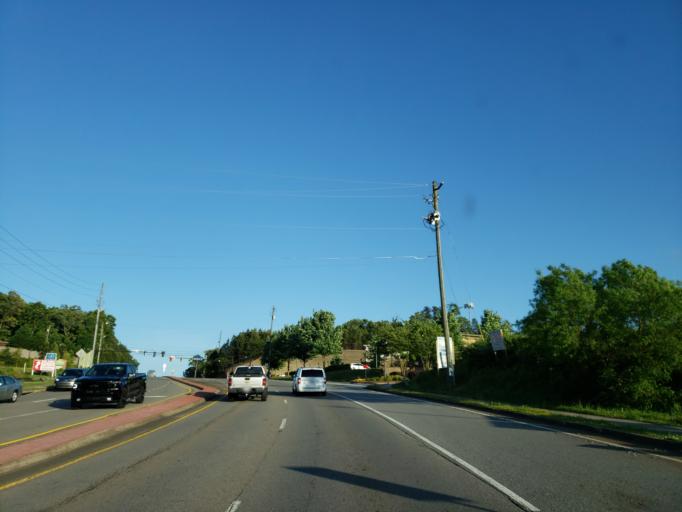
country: US
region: Georgia
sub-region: Cherokee County
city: Holly Springs
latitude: 34.1727
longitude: -84.5486
